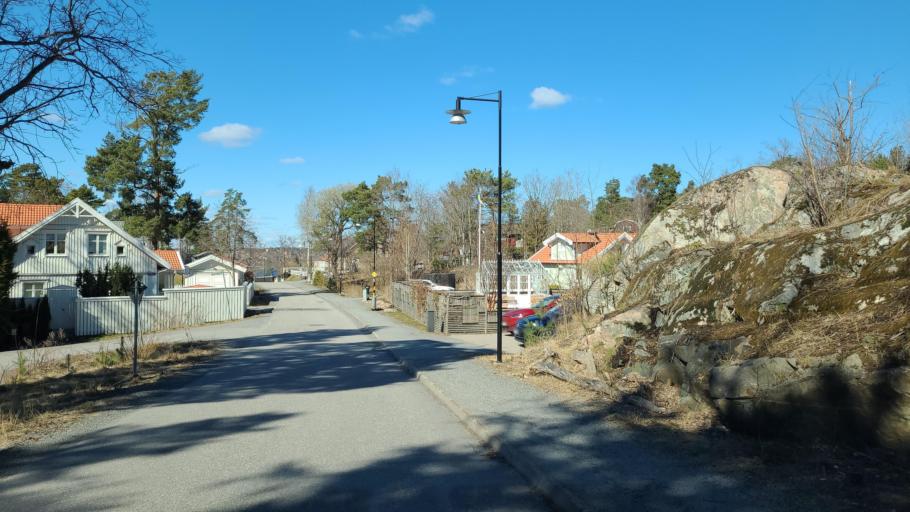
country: SE
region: Stockholm
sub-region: Lidingo
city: Brevik
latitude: 59.3279
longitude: 18.2219
